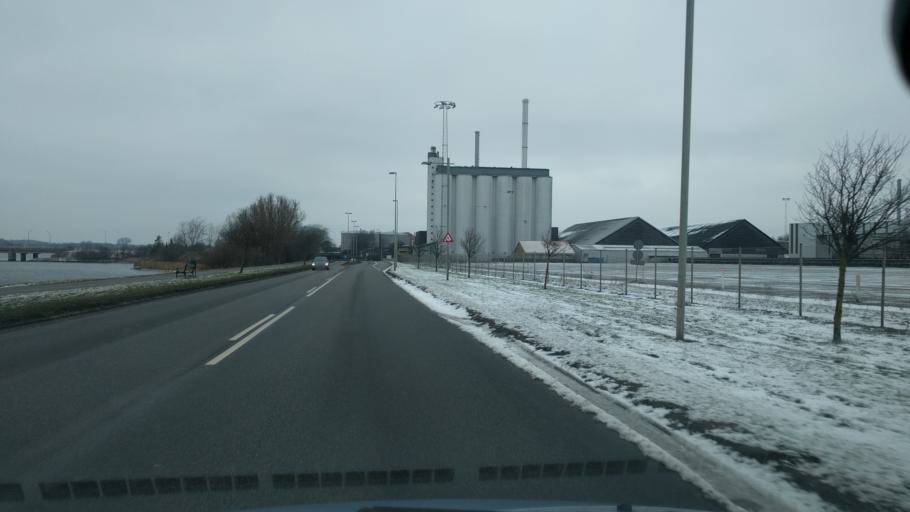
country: DK
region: Zealand
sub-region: Guldborgsund Kommune
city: Nykobing Falster
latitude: 54.7571
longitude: 11.8726
